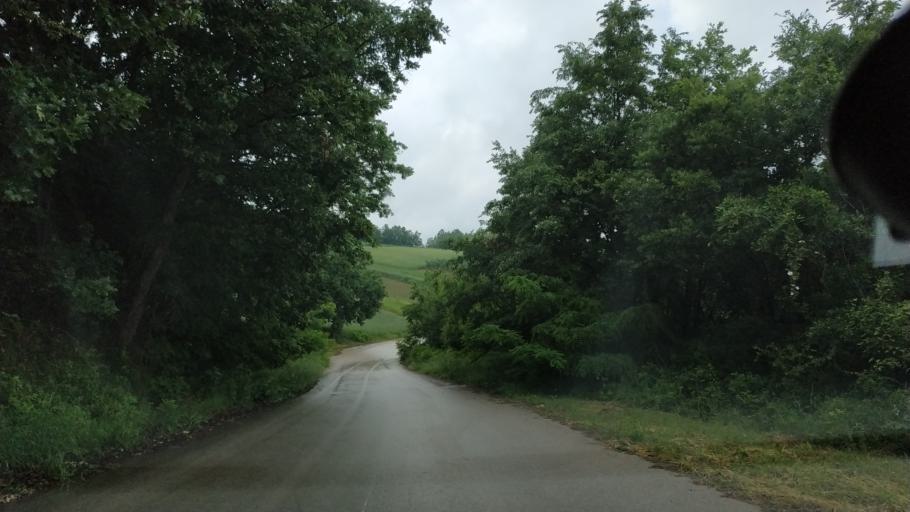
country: RS
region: Central Serbia
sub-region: Toplicki Okrug
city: Prokuplje
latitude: 43.4145
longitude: 21.5537
